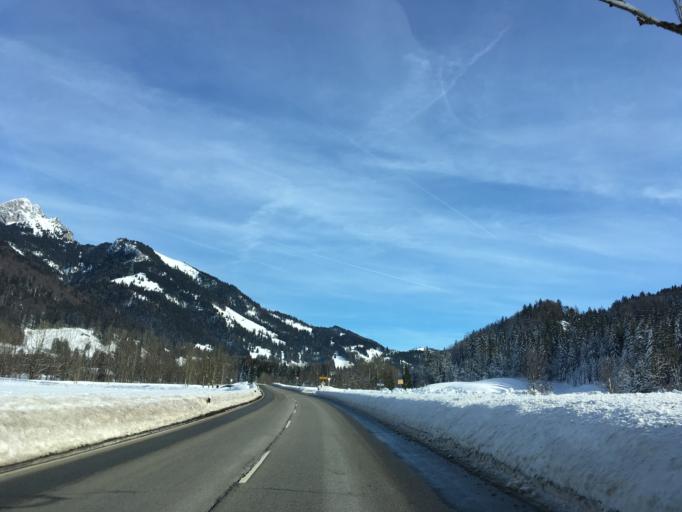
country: DE
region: Bavaria
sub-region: Upper Bavaria
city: Fischbachau
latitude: 47.6912
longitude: 11.9633
